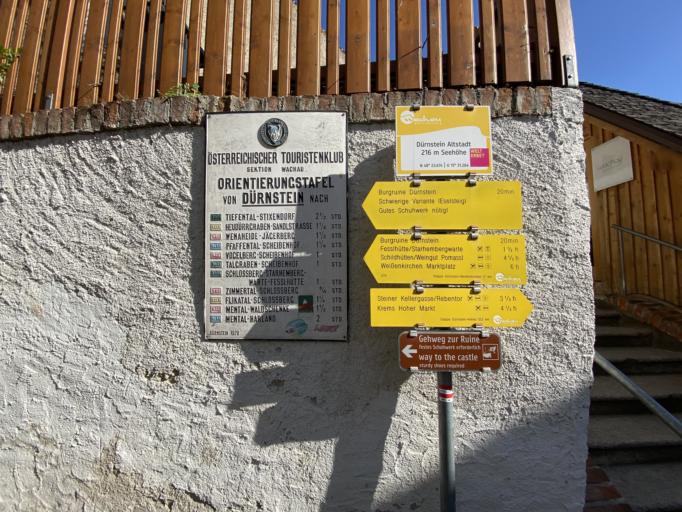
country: AT
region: Lower Austria
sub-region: Politischer Bezirk Krems
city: Durnstein
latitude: 48.3947
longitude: 15.5210
